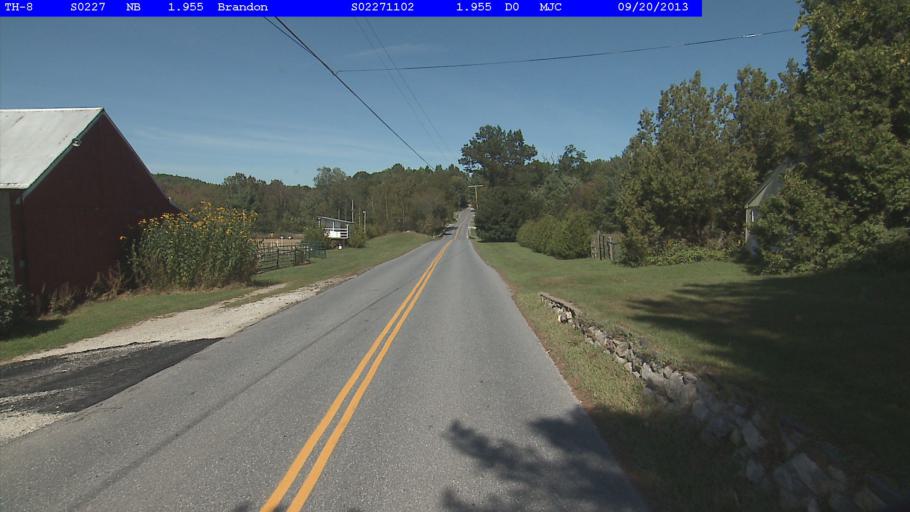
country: US
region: Vermont
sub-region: Rutland County
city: Brandon
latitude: 43.8025
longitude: -73.0558
